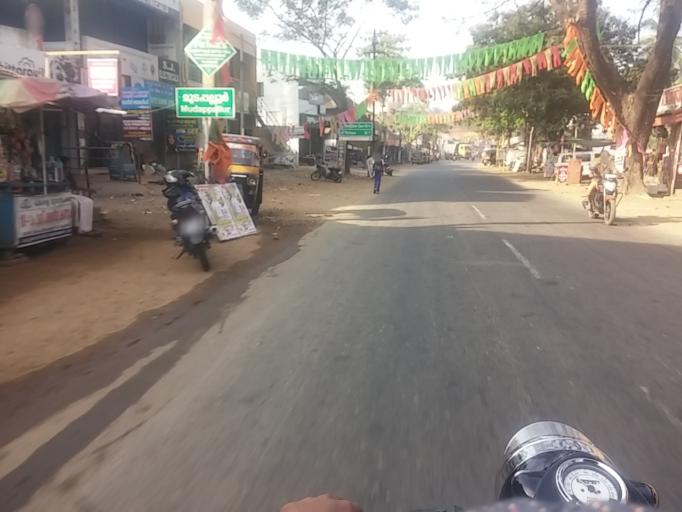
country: IN
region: Kerala
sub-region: Thrissur District
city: Chelakara
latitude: 10.5929
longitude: 76.5205
